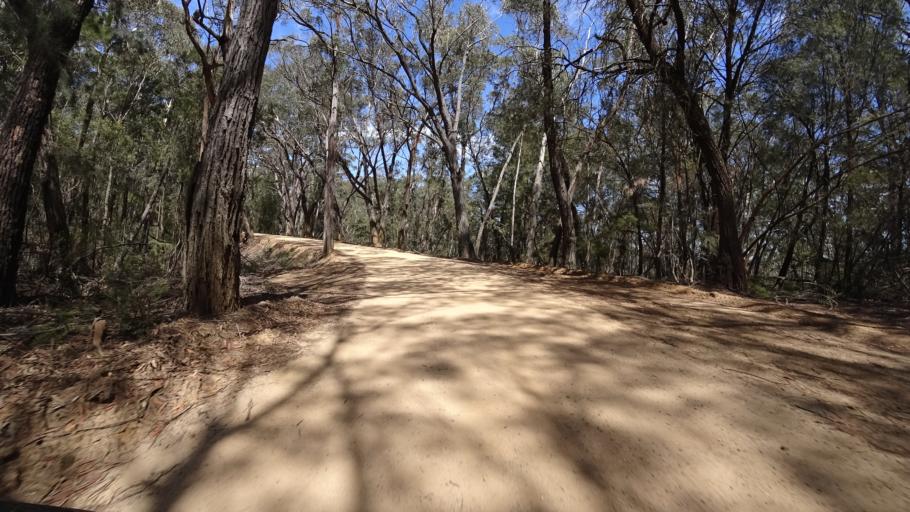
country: AU
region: New South Wales
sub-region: Lithgow
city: Lithgow
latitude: -33.2727
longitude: 150.2252
